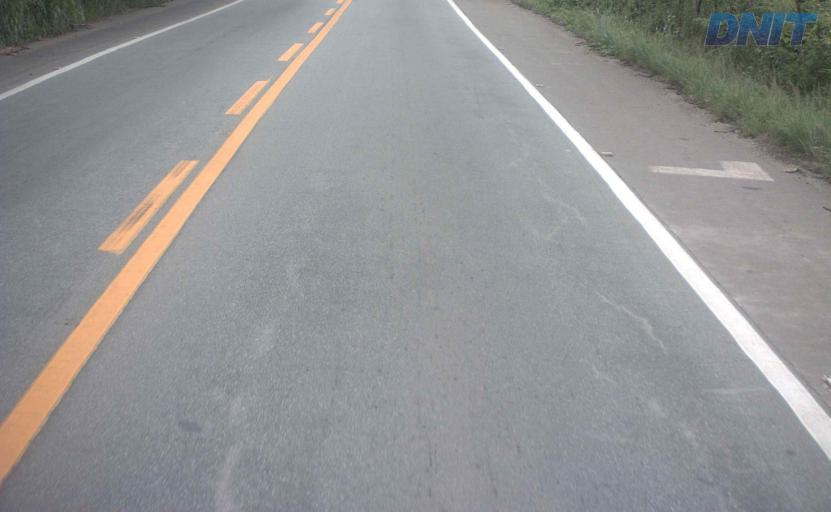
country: BR
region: Minas Gerais
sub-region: Timoteo
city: Timoteo
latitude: -19.5524
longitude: -42.7072
